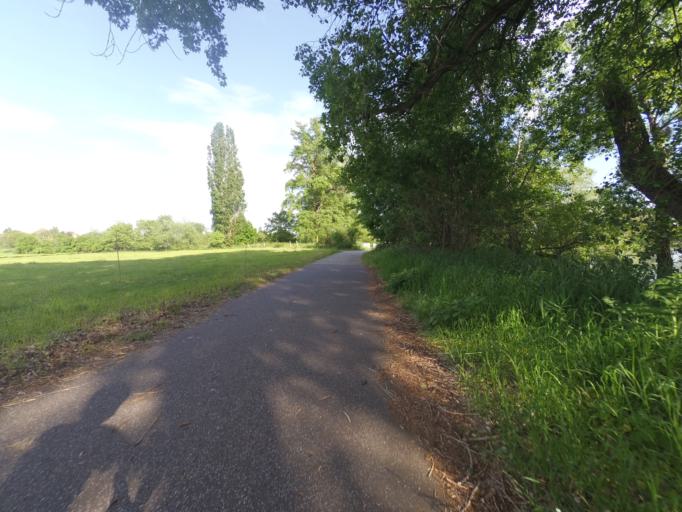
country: DE
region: Saxony
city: Radebeul
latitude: 51.0942
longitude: 13.6528
